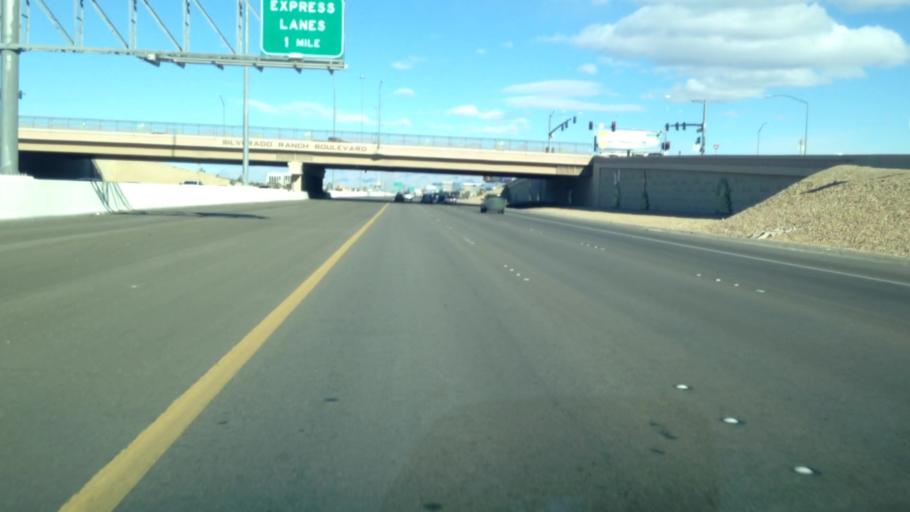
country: US
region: Nevada
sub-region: Clark County
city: Enterprise
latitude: 36.0119
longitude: -115.1803
